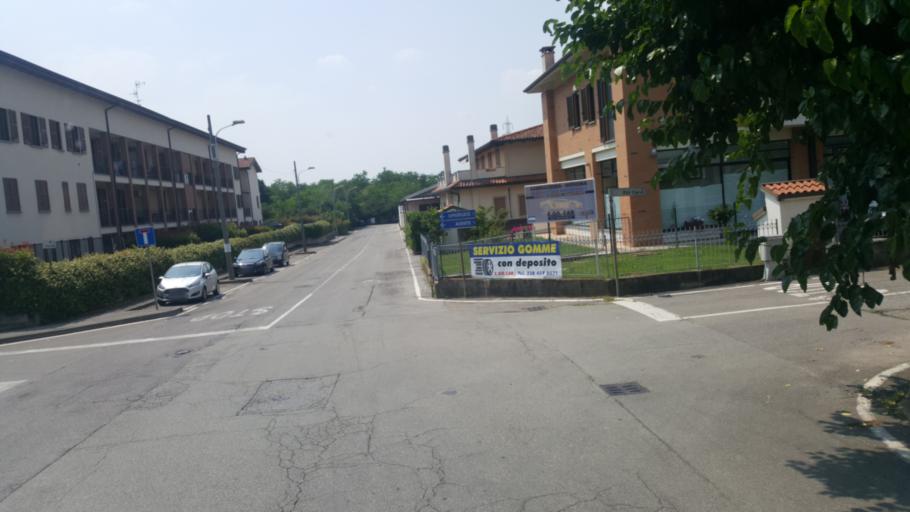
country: IT
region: Lombardy
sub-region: Provincia di Monza e Brianza
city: Burago di Molgora
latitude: 45.5987
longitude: 9.3768
